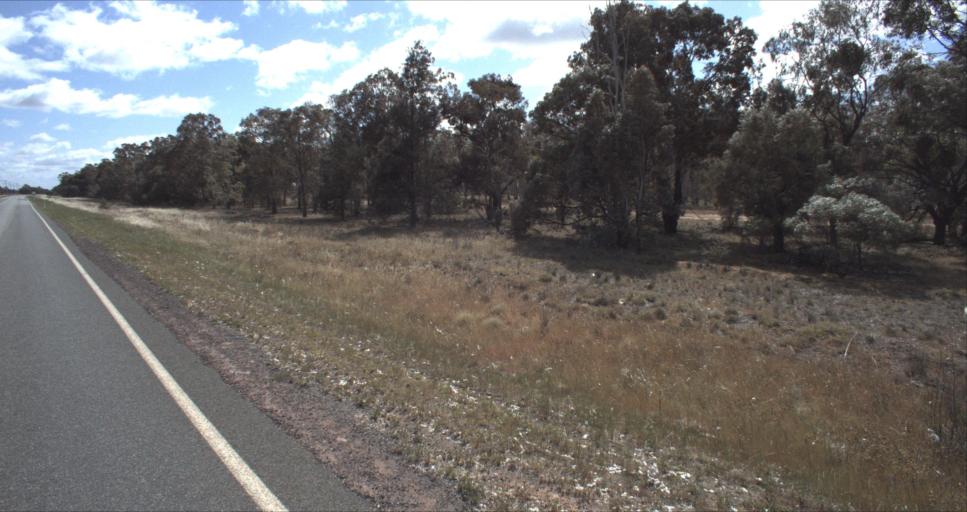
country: AU
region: New South Wales
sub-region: Murrumbidgee Shire
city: Darlington Point
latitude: -34.5852
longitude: 146.1644
